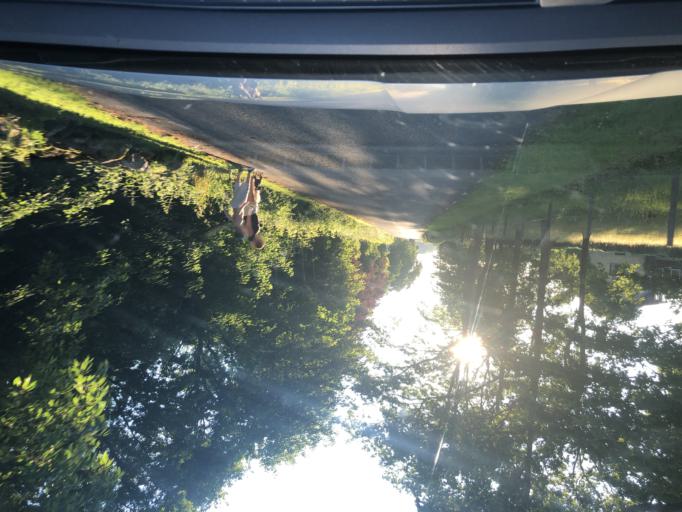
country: SE
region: Blekinge
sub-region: Karlshamns Kommun
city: Morrum
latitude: 56.1354
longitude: 14.6654
